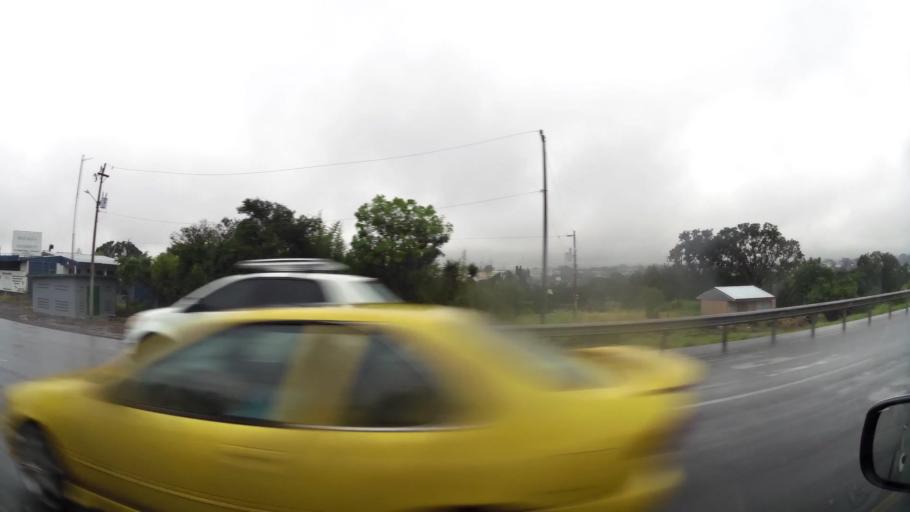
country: CR
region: Alajuela
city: Alajuela
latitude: 9.9987
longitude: -84.2098
